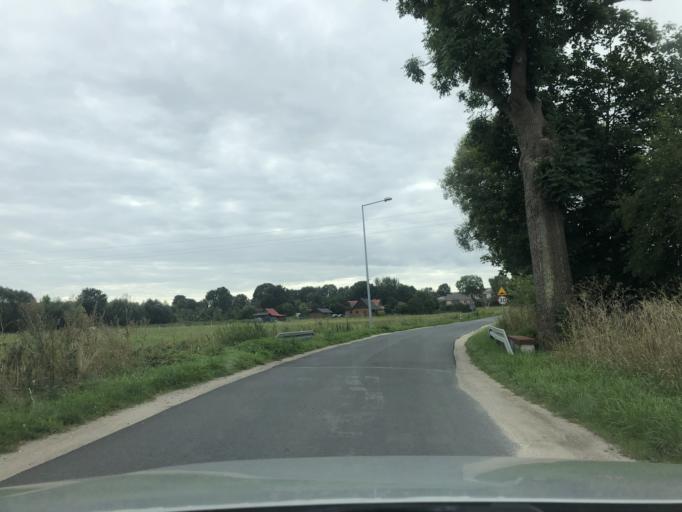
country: PL
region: Greater Poland Voivodeship
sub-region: Powiat pilski
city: Pila
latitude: 53.2688
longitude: 16.6903
